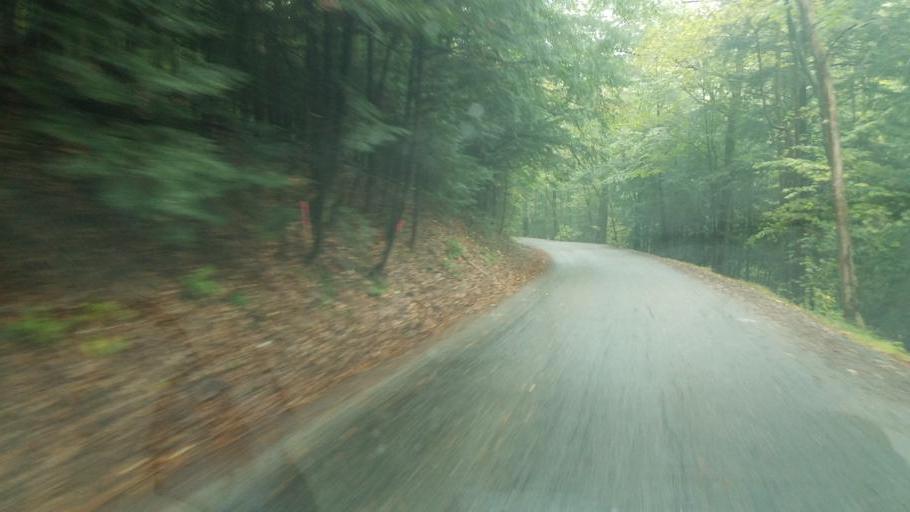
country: US
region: Ohio
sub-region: Ashland County
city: Loudonville
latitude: 40.6164
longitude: -82.3126
